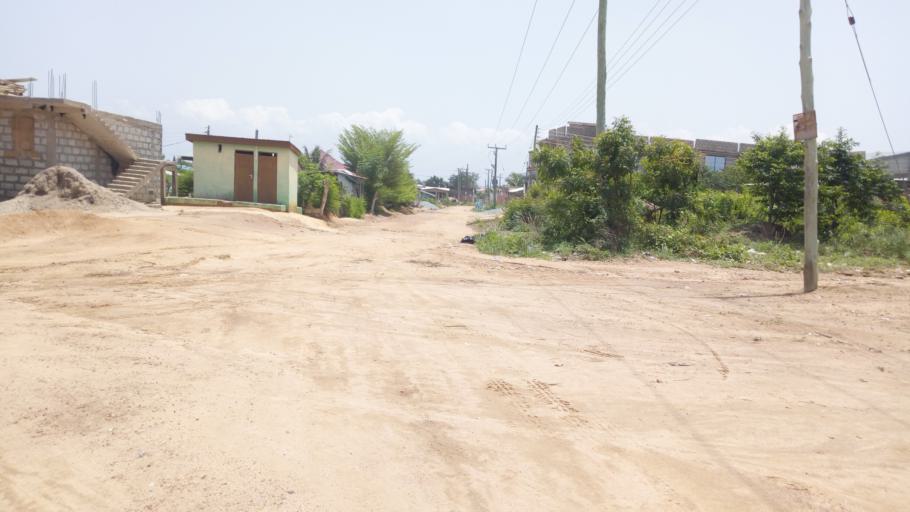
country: GH
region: Central
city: Kasoa
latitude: 5.5028
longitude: -0.4500
